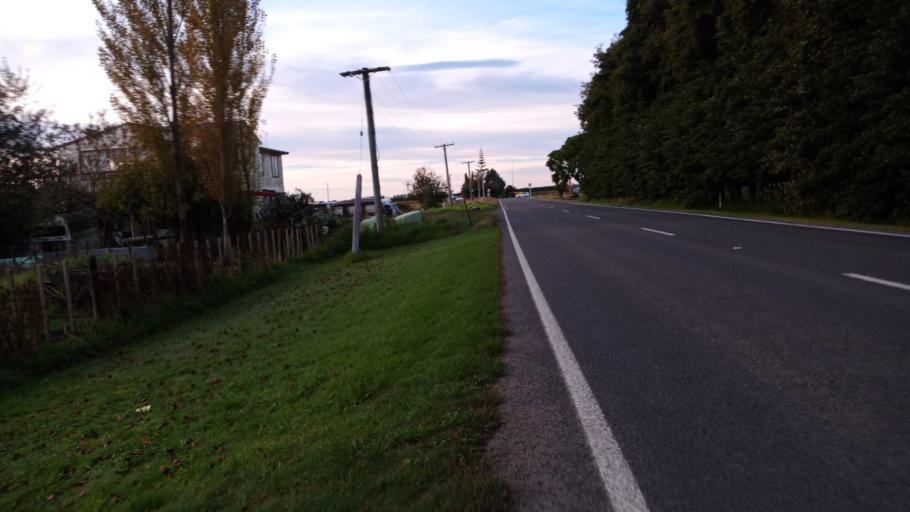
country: NZ
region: Gisborne
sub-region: Gisborne District
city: Gisborne
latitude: -38.6525
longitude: 177.9525
